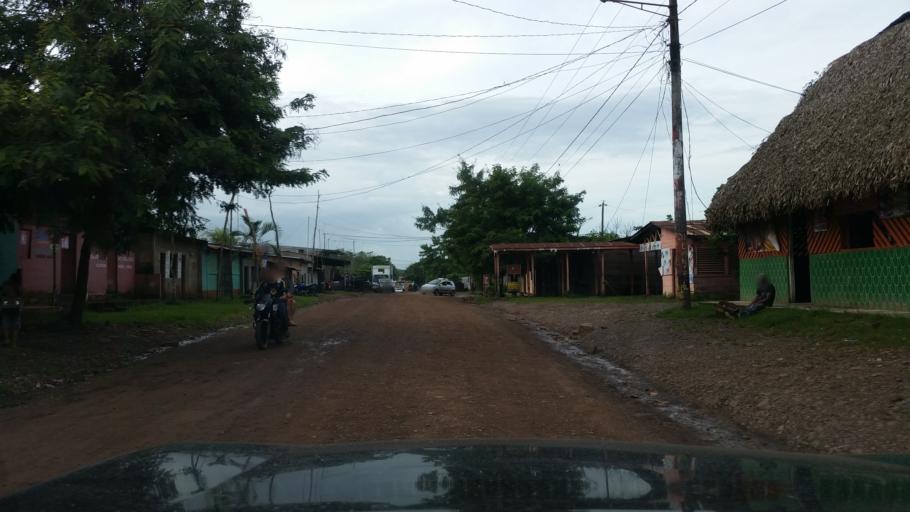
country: NI
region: Matagalpa
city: Rio Blanco
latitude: 13.1800
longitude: -84.9514
